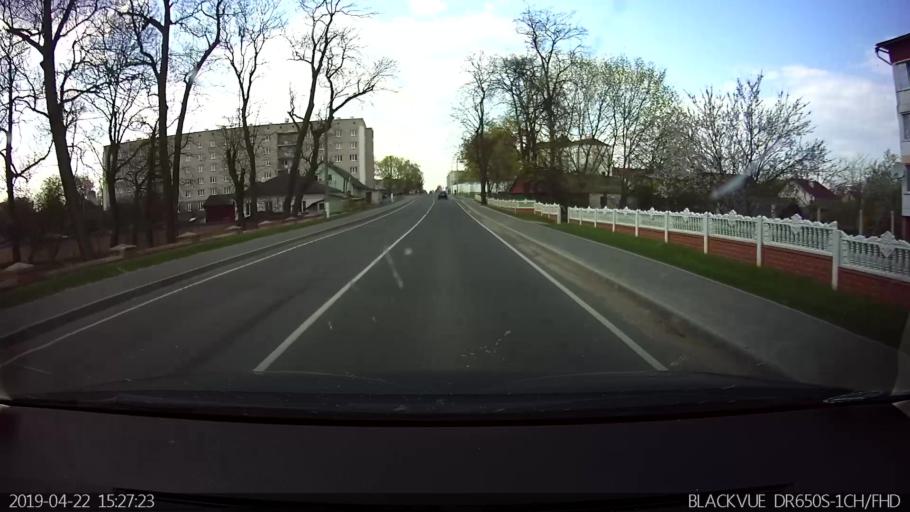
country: BY
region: Brest
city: Vysokaye
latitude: 52.3703
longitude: 23.3723
